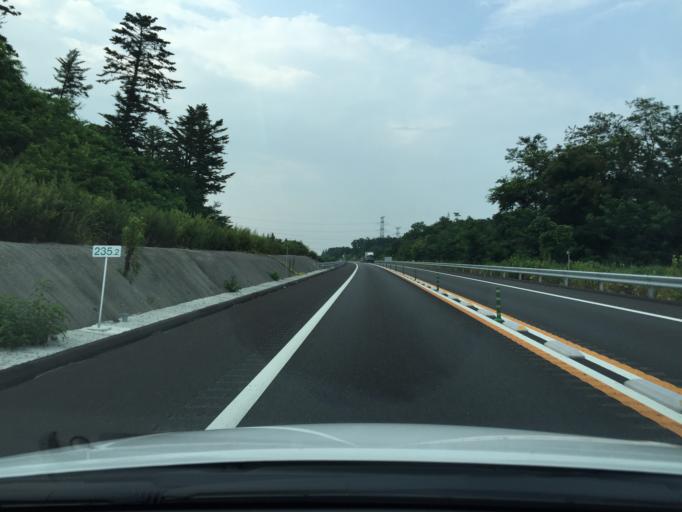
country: JP
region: Fukushima
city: Namie
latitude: 37.5198
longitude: 140.9440
